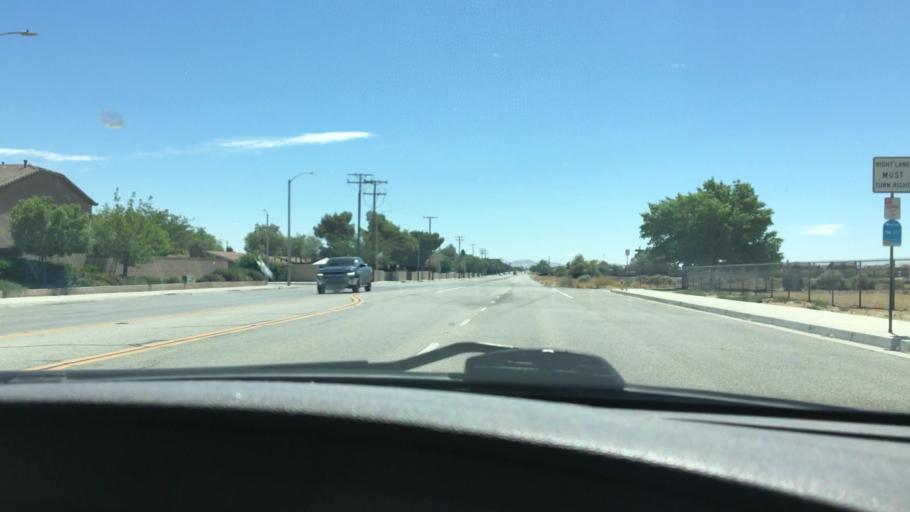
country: US
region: California
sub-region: Los Angeles County
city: Lancaster
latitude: 34.6751
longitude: -118.0910
